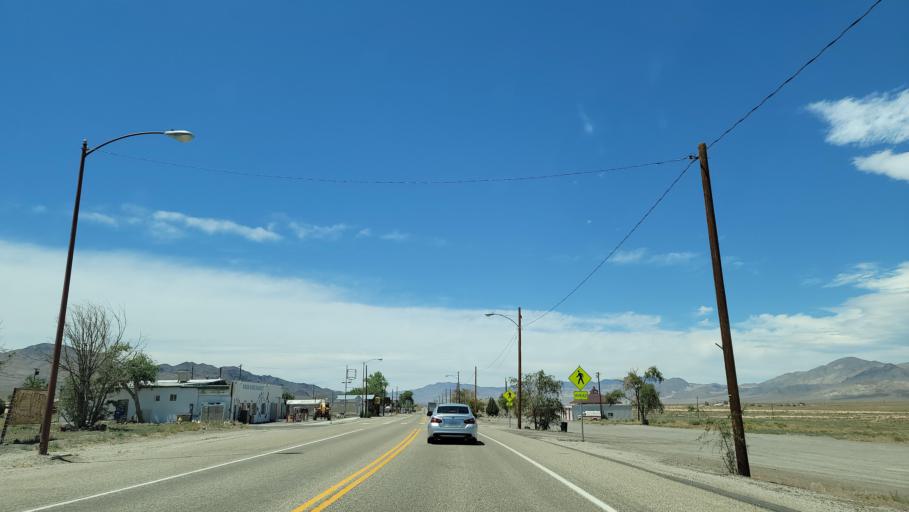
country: US
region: Nevada
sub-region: Mineral County
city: Hawthorne
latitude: 38.3892
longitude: -118.1078
